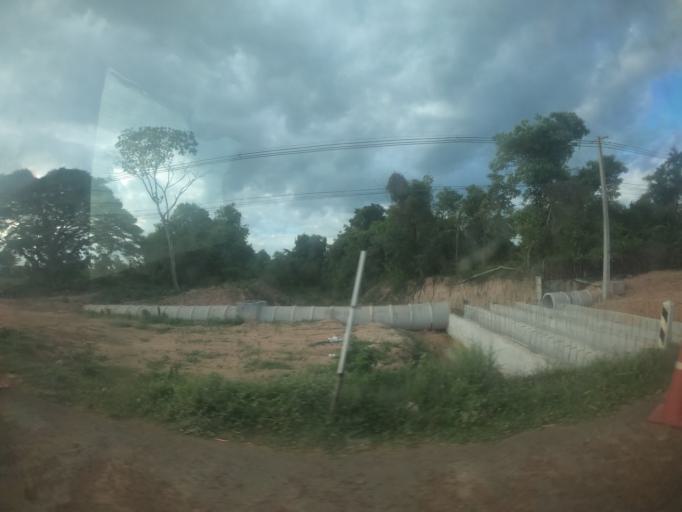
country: TH
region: Surin
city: Kap Choeng
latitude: 14.4563
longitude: 103.6777
